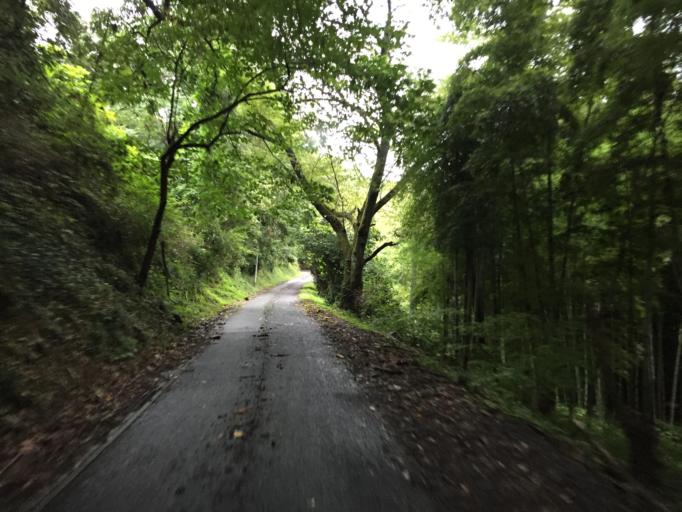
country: JP
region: Fukushima
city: Fukushima-shi
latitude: 37.7659
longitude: 140.5212
